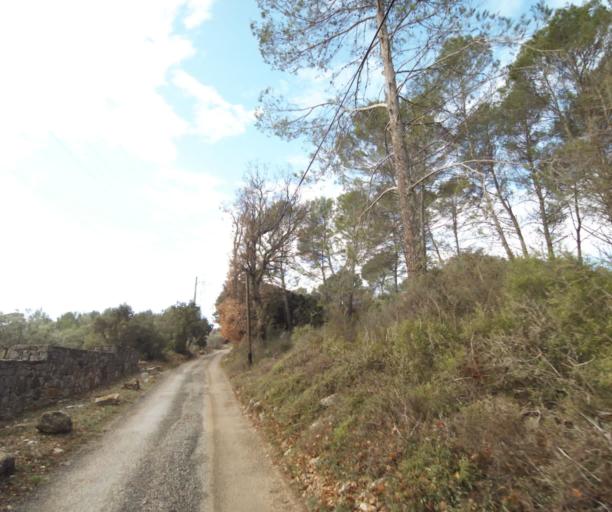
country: FR
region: Provence-Alpes-Cote d'Azur
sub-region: Departement du Var
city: Trans-en-Provence
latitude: 43.4999
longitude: 6.4678
